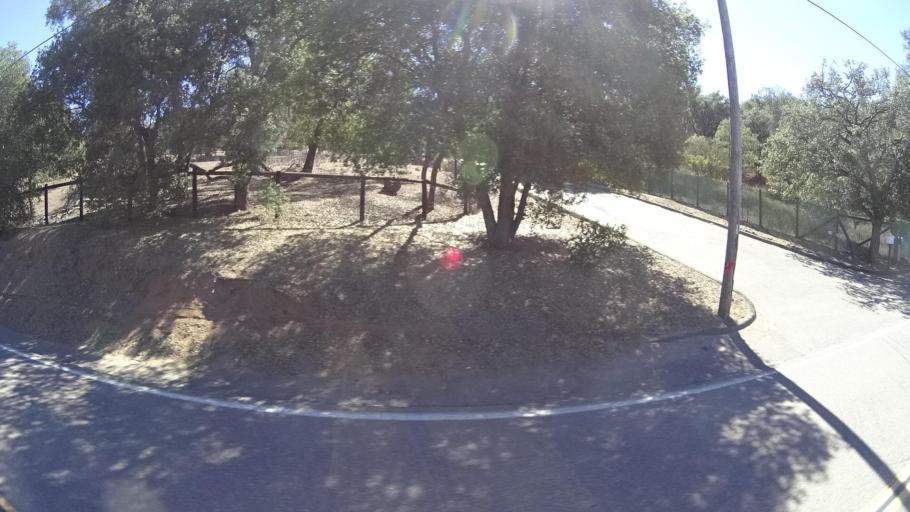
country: US
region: California
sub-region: San Diego County
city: Descanso
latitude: 32.7889
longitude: -116.6633
